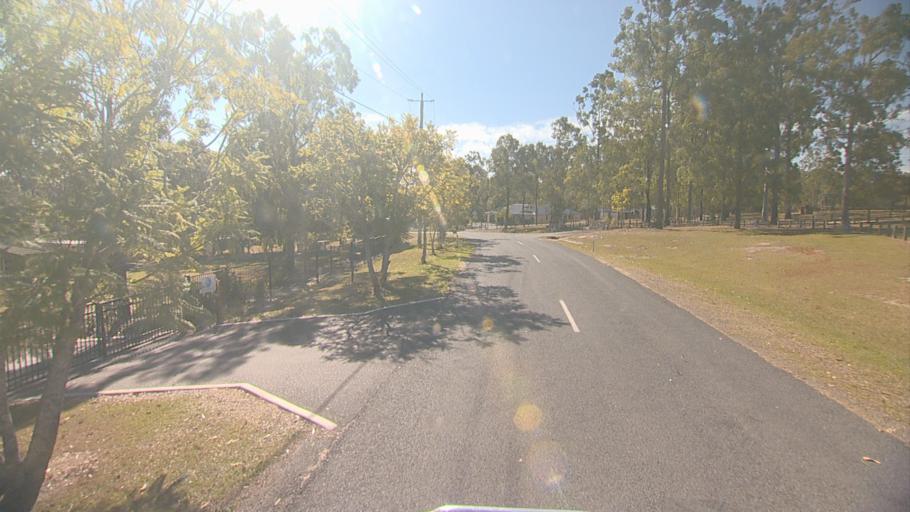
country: AU
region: Queensland
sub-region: Logan
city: North Maclean
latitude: -27.7270
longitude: 152.9621
